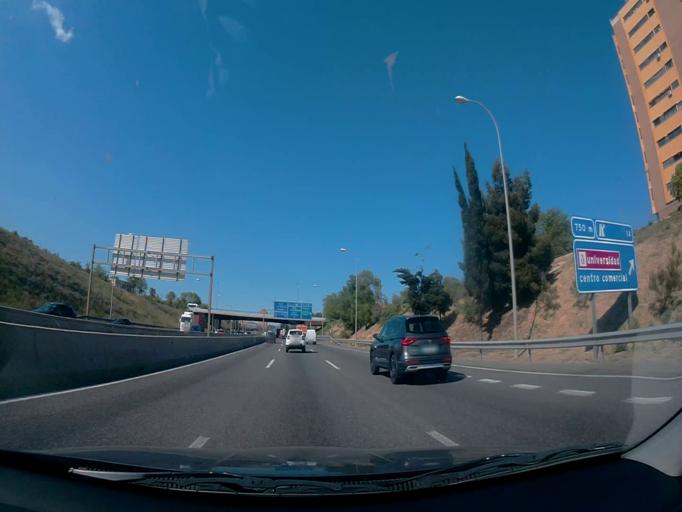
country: ES
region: Madrid
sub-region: Provincia de Madrid
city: Vicalvaro
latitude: 40.3971
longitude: -3.6272
